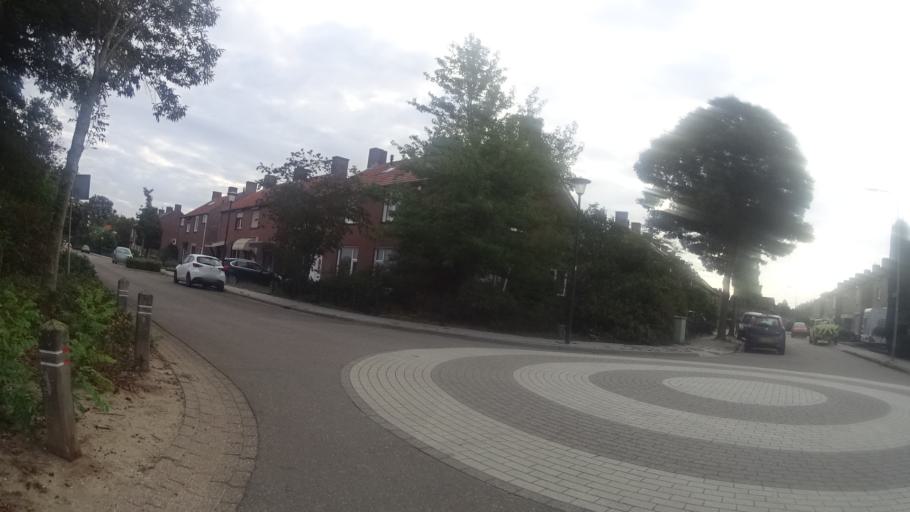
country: NL
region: Limburg
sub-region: Gemeente Venlo
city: Arcen
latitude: 51.4465
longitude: 6.1676
